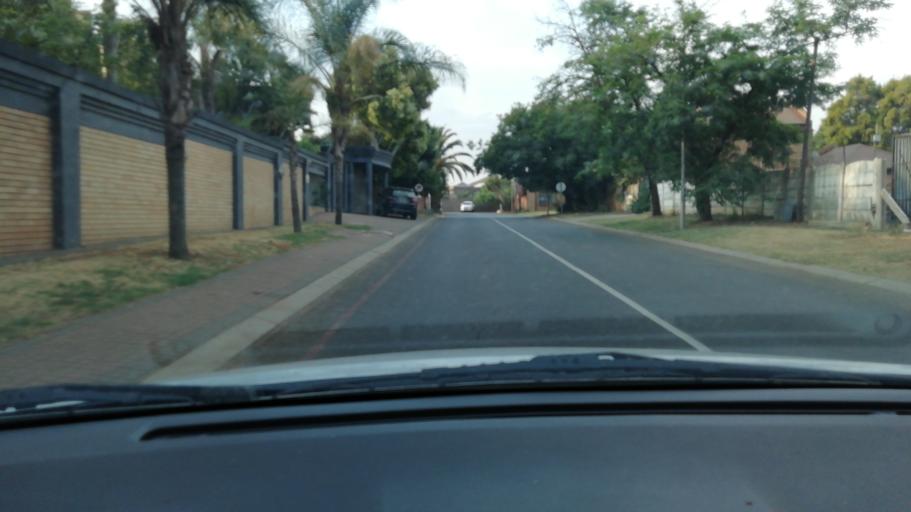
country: ZA
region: Gauteng
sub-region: Ekurhuleni Metropolitan Municipality
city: Boksburg
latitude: -26.1880
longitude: 28.2834
